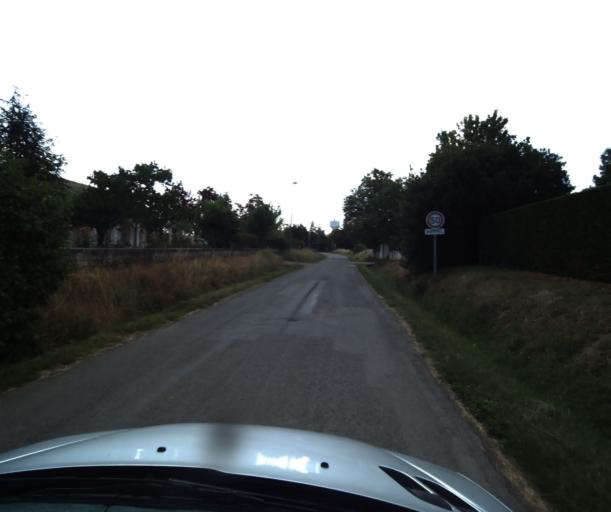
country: FR
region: Midi-Pyrenees
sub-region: Departement du Tarn-et-Garonne
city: Finhan
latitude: 43.9133
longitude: 1.2687
